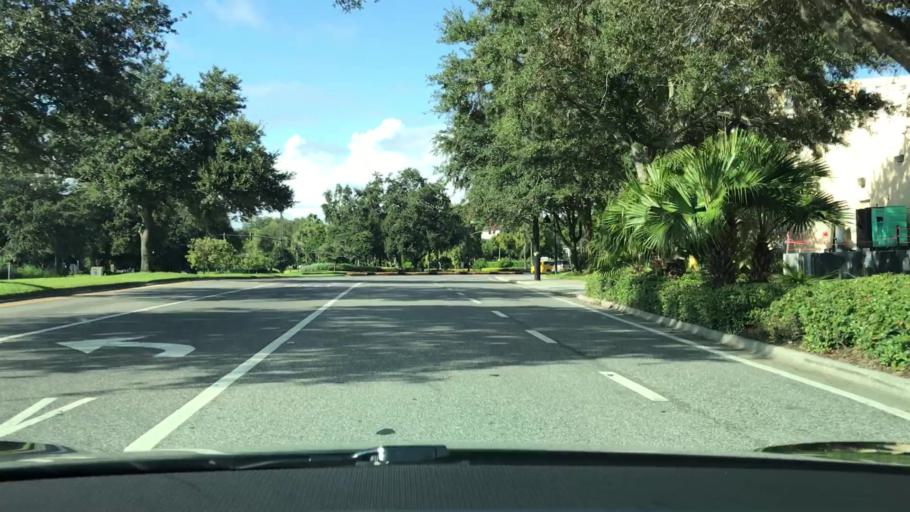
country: US
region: Florida
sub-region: Orange County
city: Doctor Phillips
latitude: 28.4311
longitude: -81.4696
